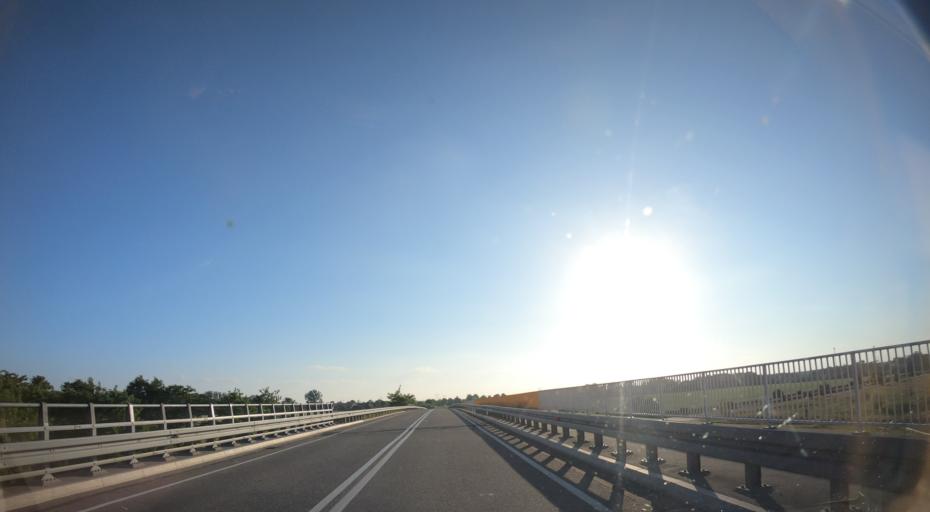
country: PL
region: Lubusz
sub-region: Powiat gorzowski
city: Jenin
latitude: 52.7794
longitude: 15.1204
